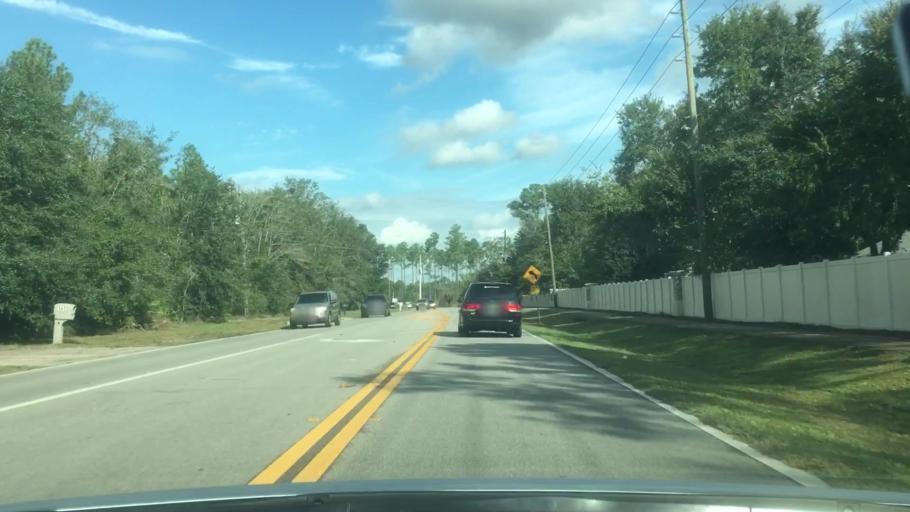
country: US
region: Florida
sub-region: Nassau County
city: Yulee
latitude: 30.4976
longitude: -81.5755
